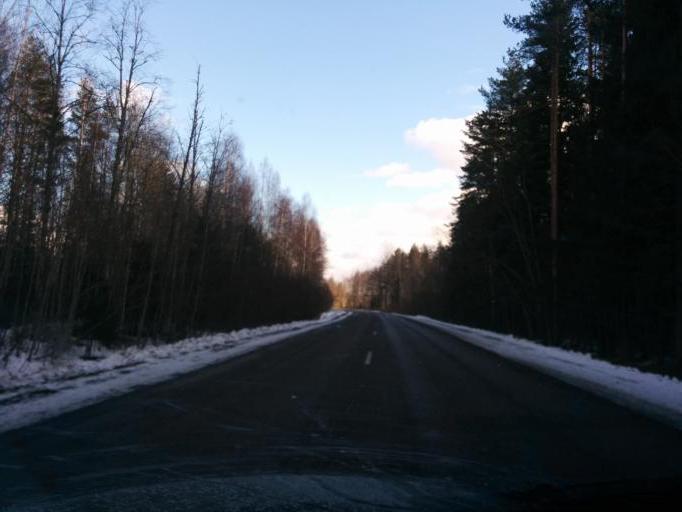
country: LV
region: Balvu Rajons
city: Balvi
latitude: 57.1789
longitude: 27.0878
